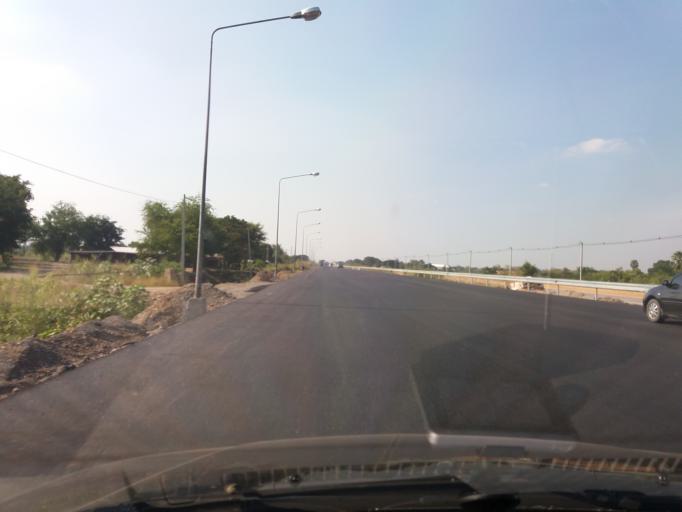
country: TH
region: Nakhon Sawan
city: Krok Phra
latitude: 15.6241
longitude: 100.1118
